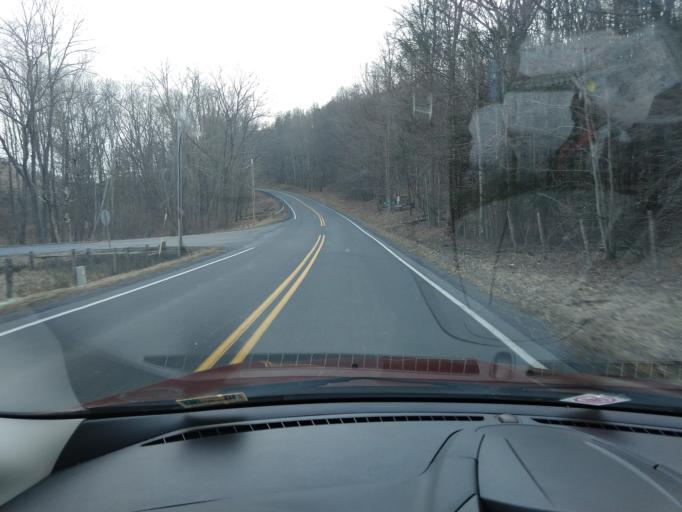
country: US
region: Virginia
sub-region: Highland County
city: Monterey
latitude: 38.4417
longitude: -79.5385
